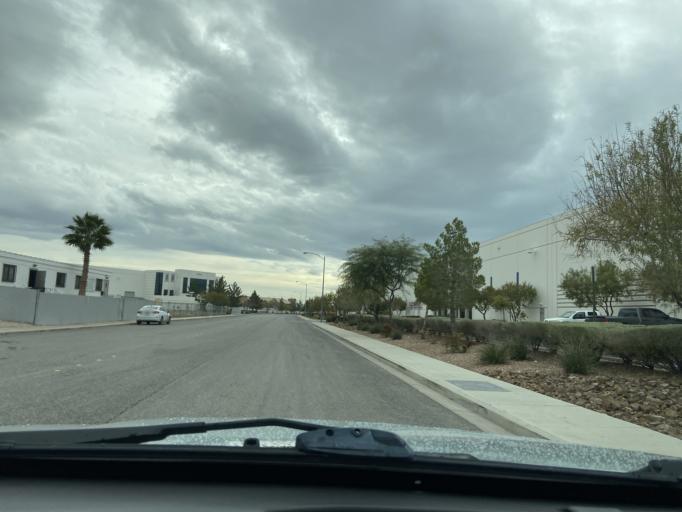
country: US
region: Nevada
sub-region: Clark County
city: Nellis Air Force Base
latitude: 36.2467
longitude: -115.1045
